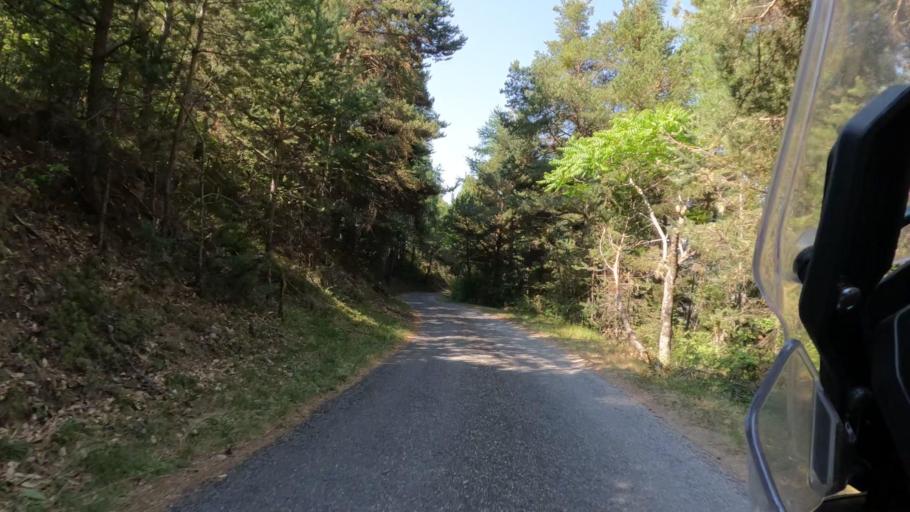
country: FR
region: Provence-Alpes-Cote d'Azur
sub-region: Departement des Hautes-Alpes
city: Embrun
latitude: 44.5953
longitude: 6.5465
